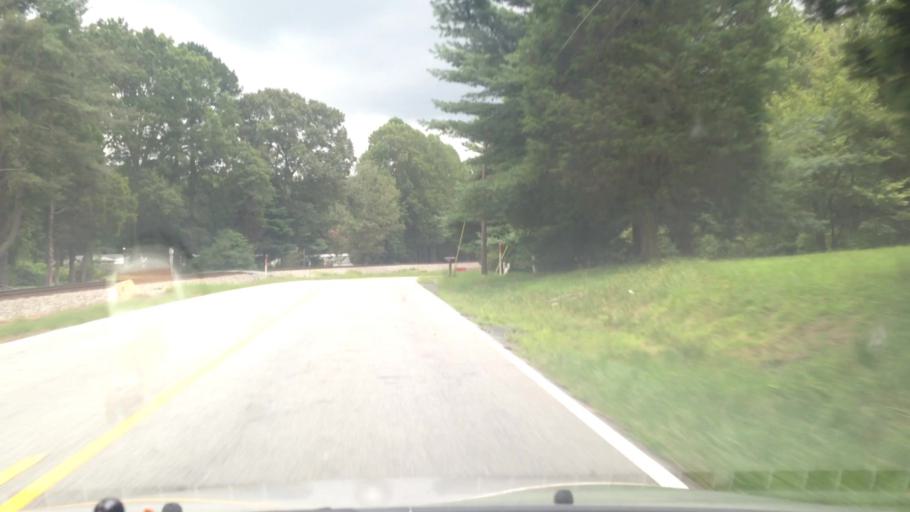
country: US
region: North Carolina
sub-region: Forsyth County
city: Walkertown
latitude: 36.2179
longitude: -80.1670
